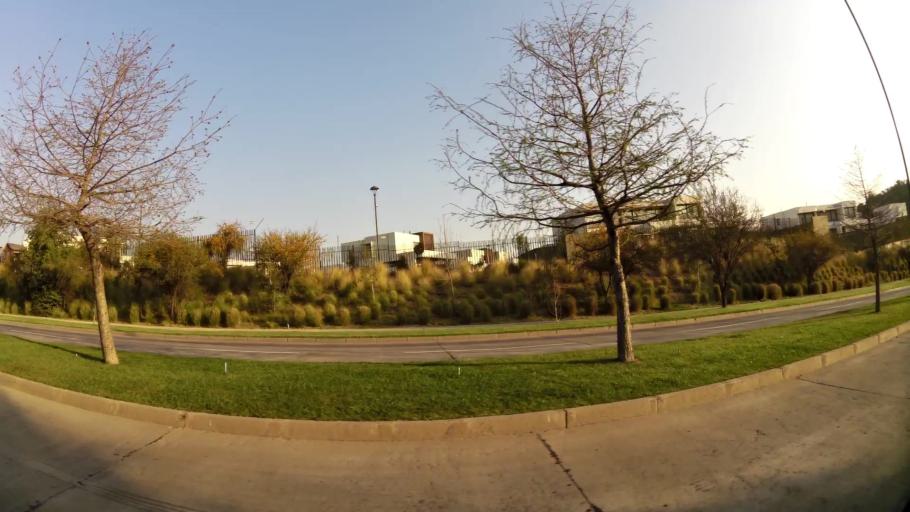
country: CL
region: Santiago Metropolitan
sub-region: Provincia de Santiago
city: Villa Presidente Frei, Nunoa, Santiago, Chile
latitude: -33.3330
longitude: -70.5081
